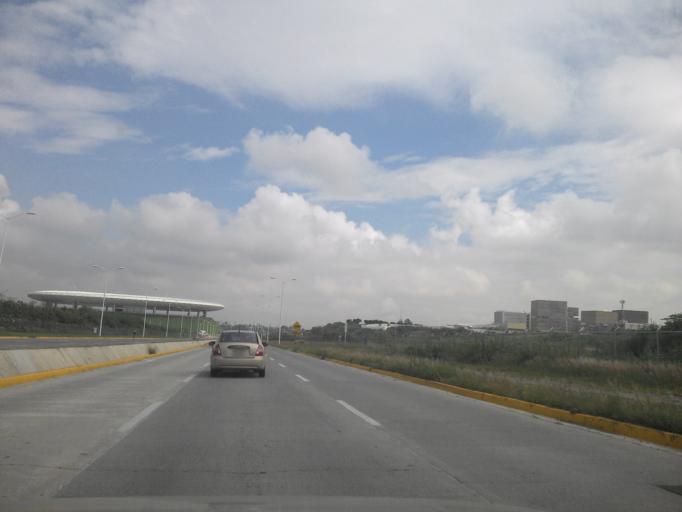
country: MX
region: Jalisco
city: Guadalajara
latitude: 20.6743
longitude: -103.4619
